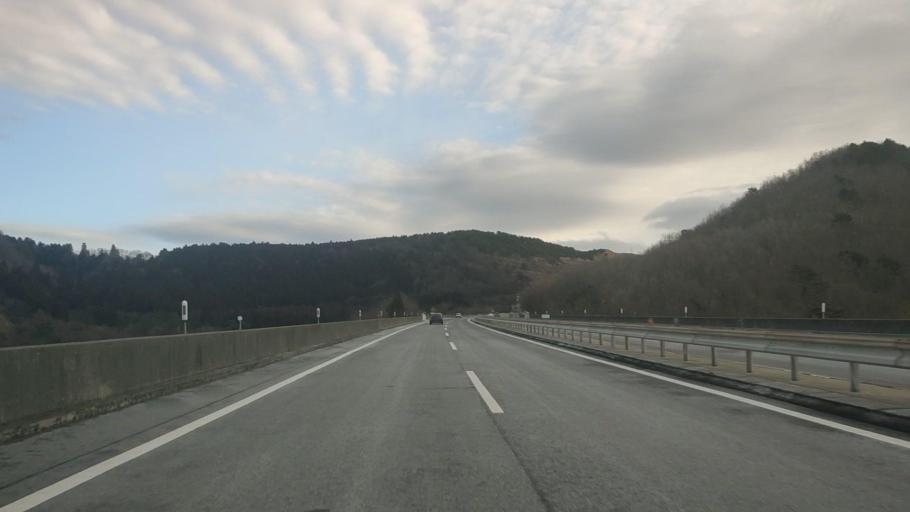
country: JP
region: Oita
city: Beppu
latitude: 33.2929
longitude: 131.3556
